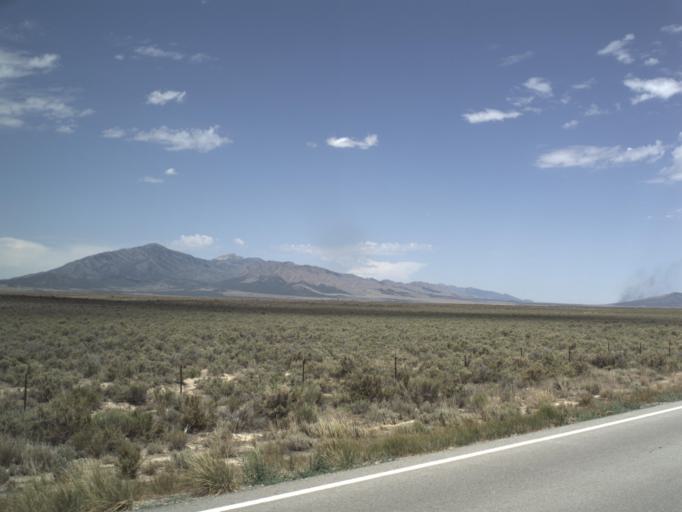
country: US
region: Utah
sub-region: Tooele County
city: Tooele
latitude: 40.2279
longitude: -112.4039
